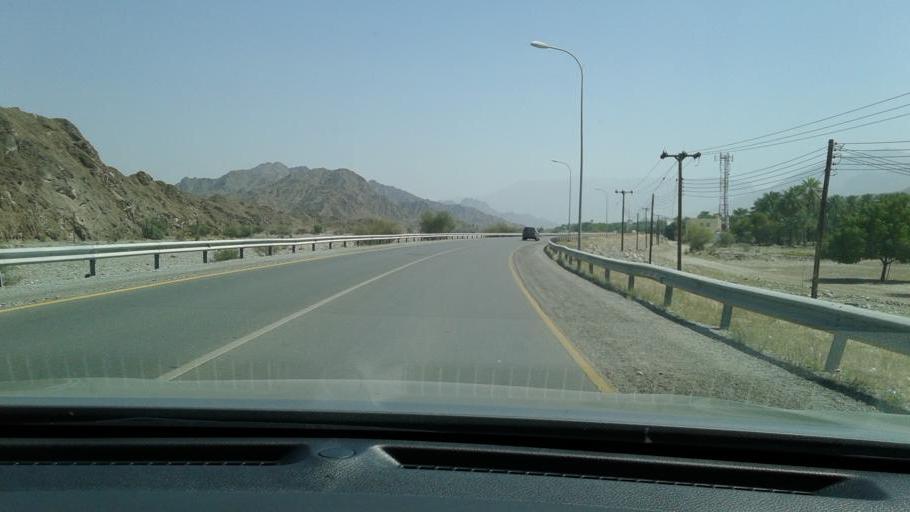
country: OM
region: Al Batinah
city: Rustaq
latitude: 23.3984
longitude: 57.4343
